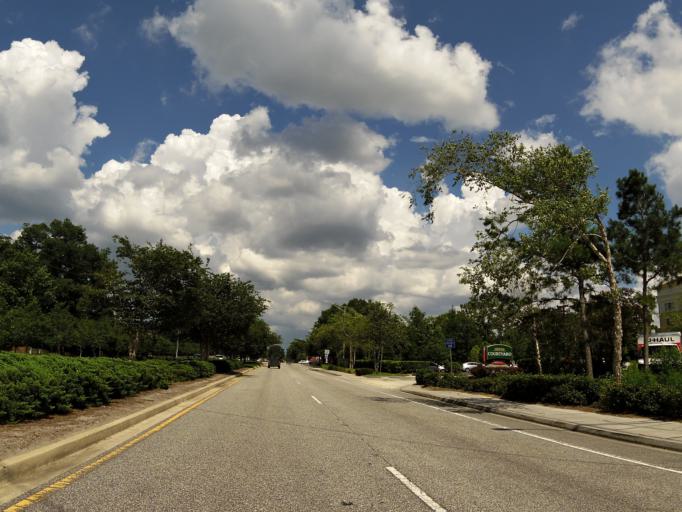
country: US
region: Florida
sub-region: Saint Johns County
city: Fruit Cove
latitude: 30.1410
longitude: -81.5353
